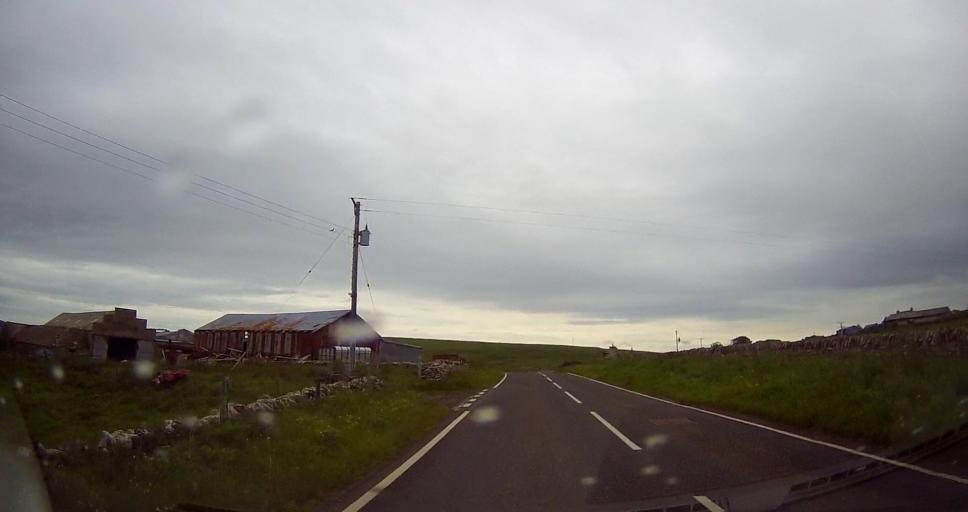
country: GB
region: Scotland
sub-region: Orkney Islands
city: Orkney
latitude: 59.1099
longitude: -3.0988
